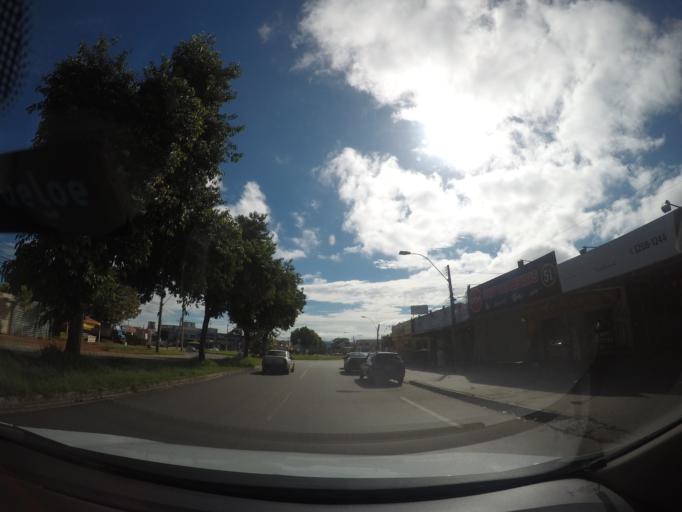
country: BR
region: Goias
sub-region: Goiania
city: Goiania
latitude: -16.6588
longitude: -49.1835
